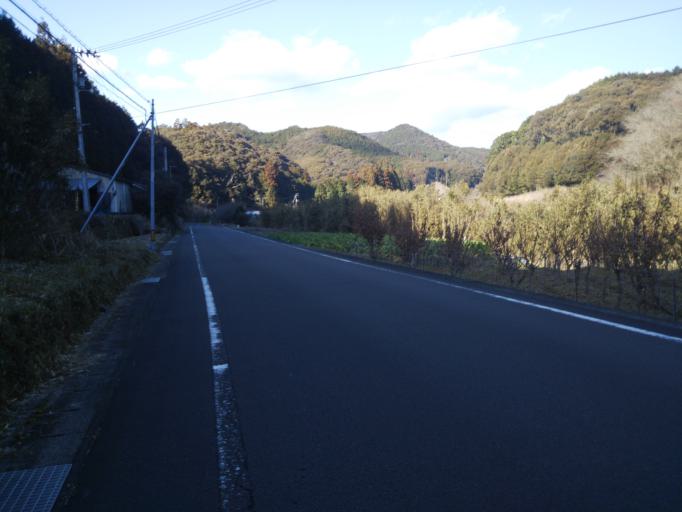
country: JP
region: Kochi
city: Nakamura
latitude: 33.0446
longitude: 132.9706
